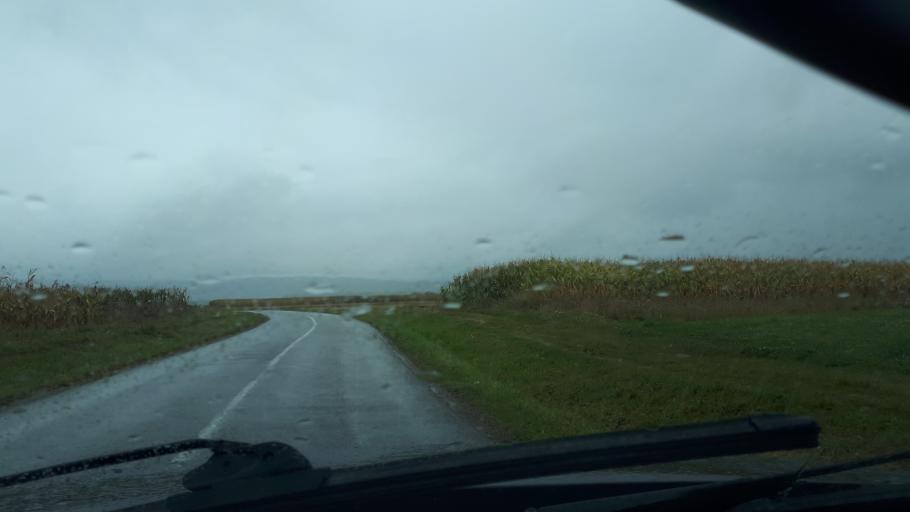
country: RO
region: Brasov
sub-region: Comuna Dragus
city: Dragus
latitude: 45.7725
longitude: 24.7764
